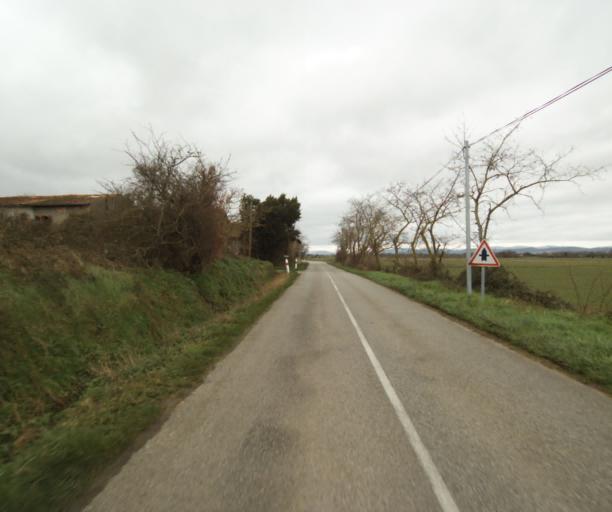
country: FR
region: Midi-Pyrenees
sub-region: Departement de l'Ariege
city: Pamiers
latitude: 43.1851
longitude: 1.6346
